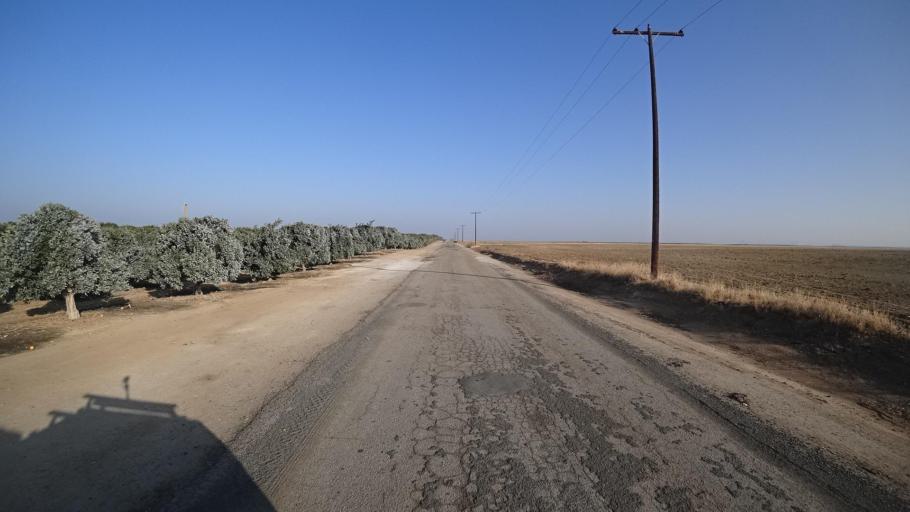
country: US
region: California
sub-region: Tulare County
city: Richgrove
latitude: 35.7637
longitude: -119.0807
